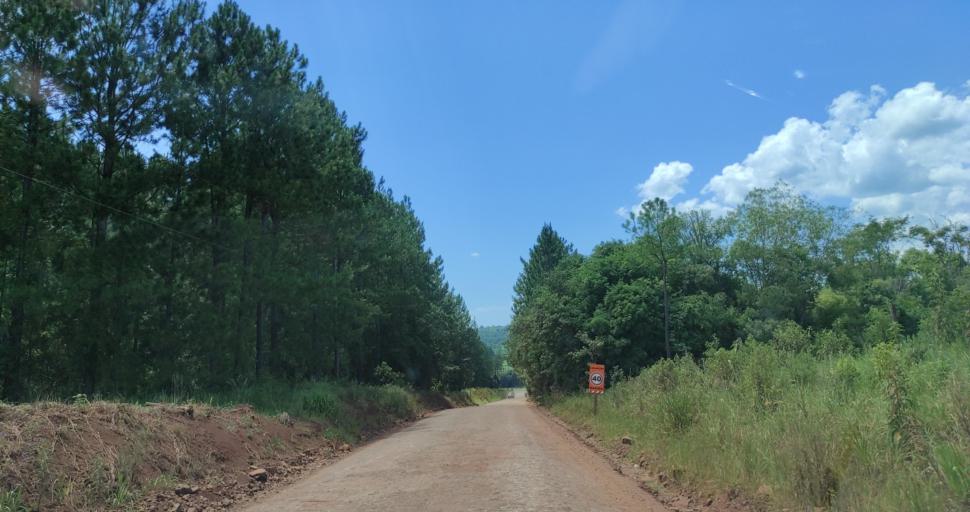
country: AR
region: Misiones
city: Ruiz de Montoya
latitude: -27.0421
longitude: -55.0077
